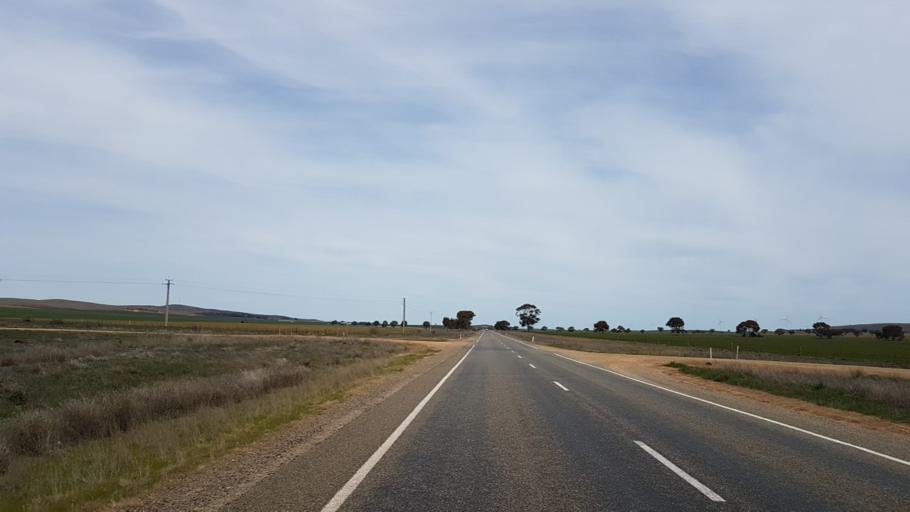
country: AU
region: South Australia
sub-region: Northern Areas
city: Jamestown
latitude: -33.0658
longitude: 138.6165
